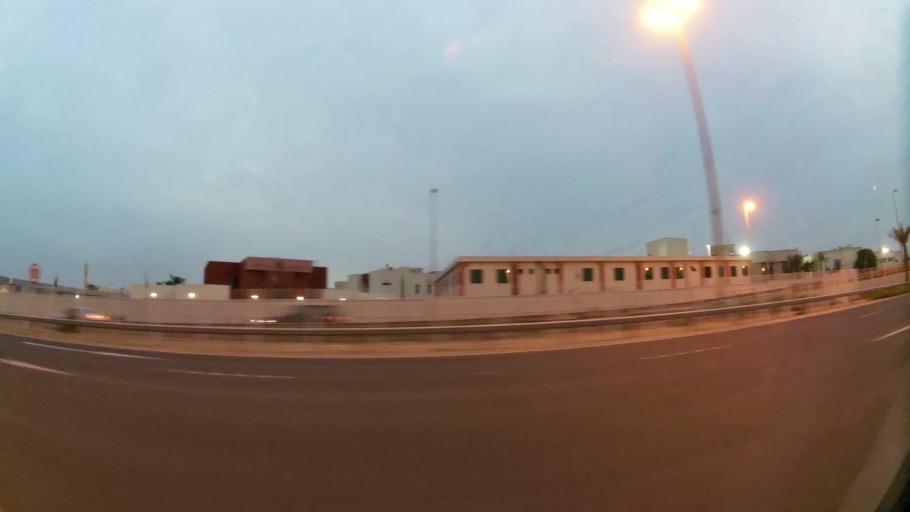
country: BH
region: Northern
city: Madinat `Isa
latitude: 26.1674
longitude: 50.5469
